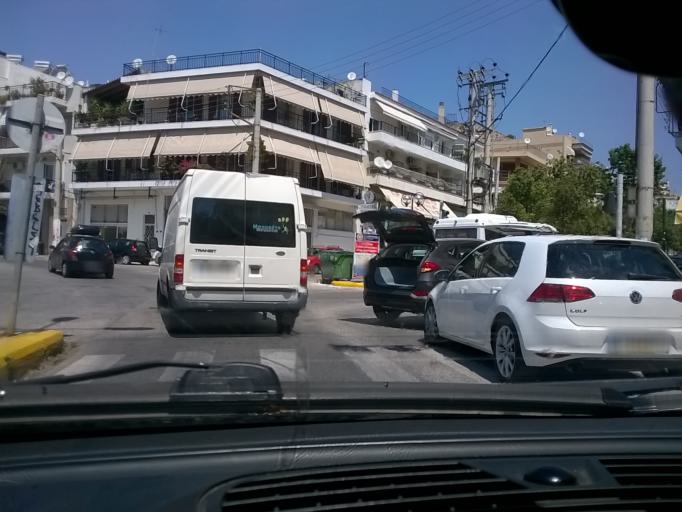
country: GR
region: Attica
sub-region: Nomarchia Athinas
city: Ymittos
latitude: 37.9461
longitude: 23.7592
